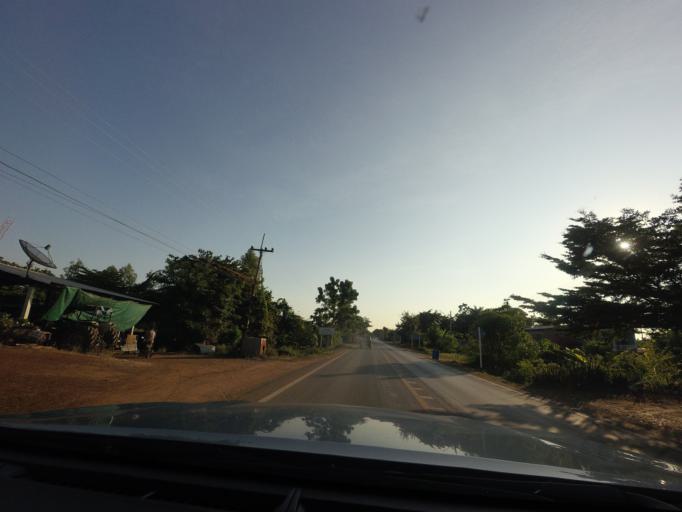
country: TH
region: Sukhothai
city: Sawankhalok
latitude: 17.3934
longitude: 99.7953
